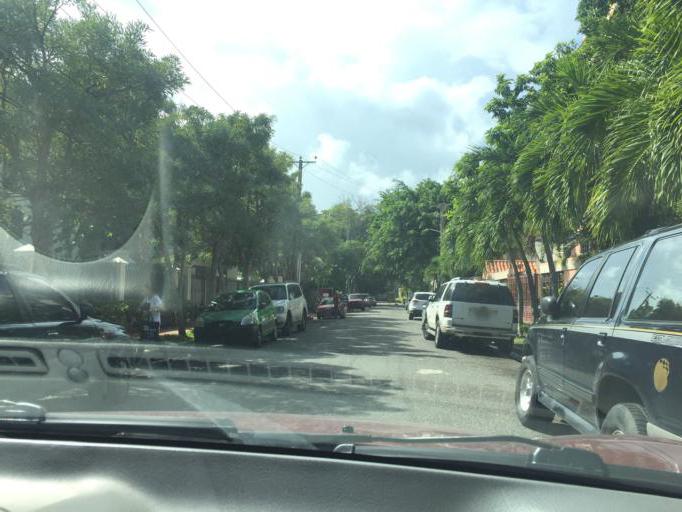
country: DO
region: Nacional
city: Ciudad Nueva
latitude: 18.4654
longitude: -69.9005
